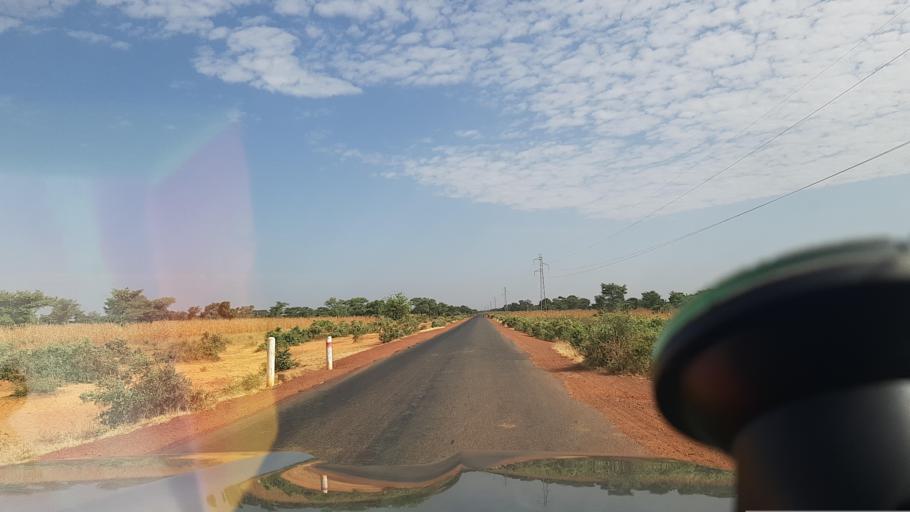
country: ML
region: Segou
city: Segou
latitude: 13.5528
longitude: -6.1158
